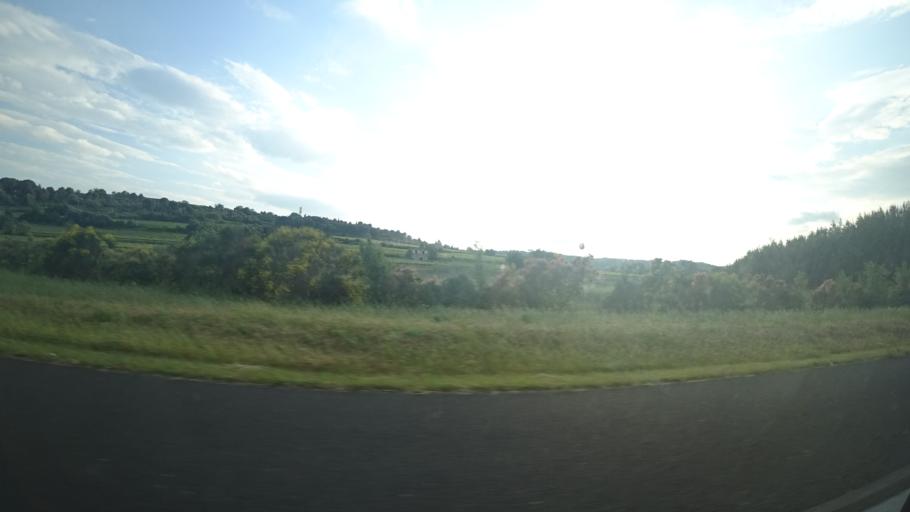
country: FR
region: Languedoc-Roussillon
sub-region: Departement de l'Herault
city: Nebian
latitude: 43.6294
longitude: 3.4490
